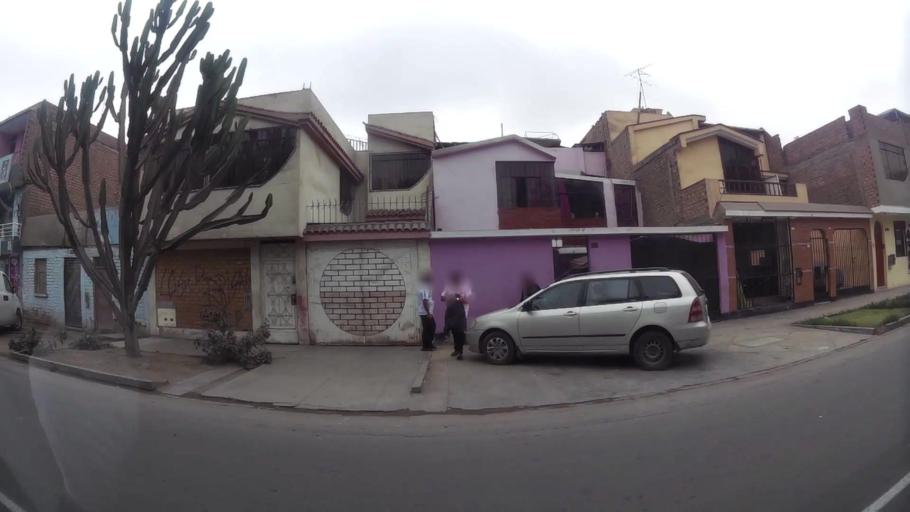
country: PE
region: Lima
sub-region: Lima
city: Independencia
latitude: -11.9742
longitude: -77.0823
